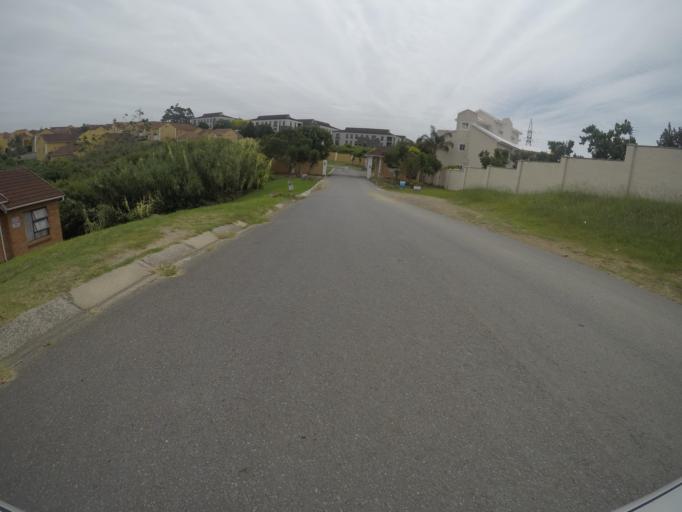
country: ZA
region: Eastern Cape
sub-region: Buffalo City Metropolitan Municipality
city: East London
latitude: -32.9592
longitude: 27.9324
